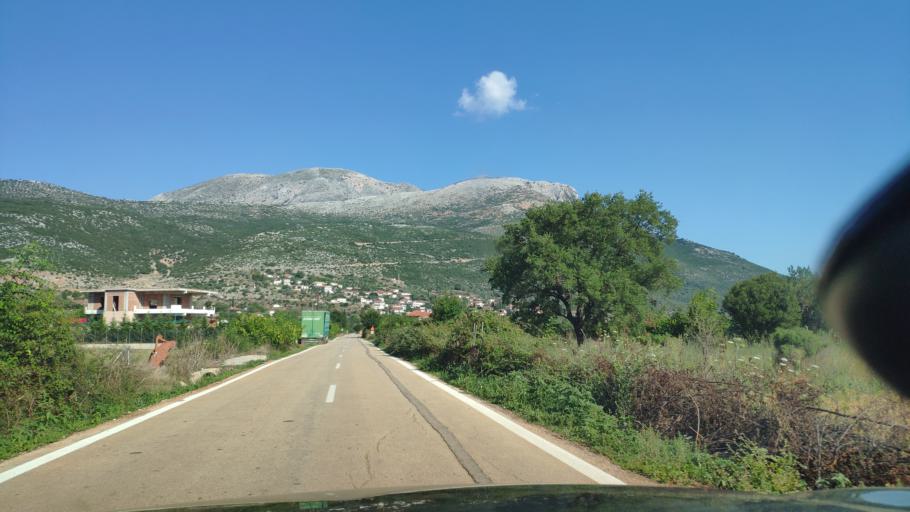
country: GR
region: West Greece
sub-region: Nomos Aitolias kai Akarnanias
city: Archontochorion
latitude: 38.7018
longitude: 21.0913
